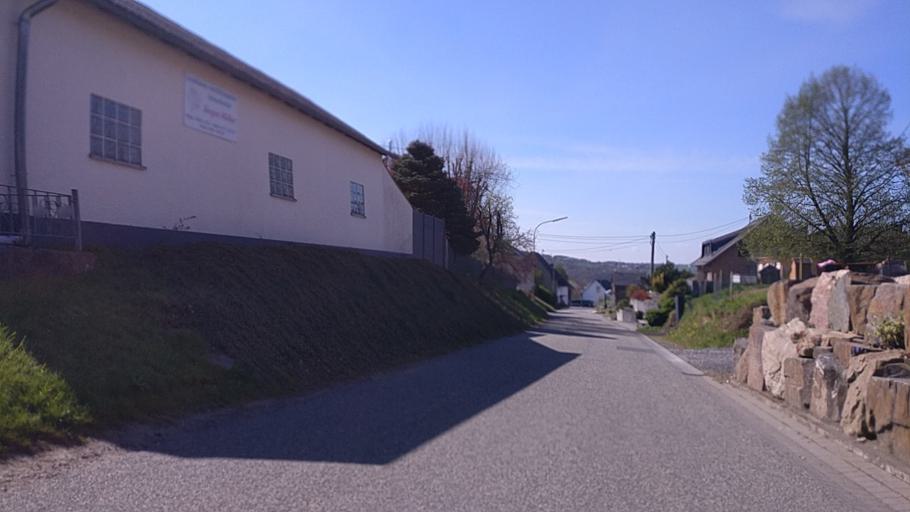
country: DE
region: Rheinland-Pfalz
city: Asbach
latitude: 50.6347
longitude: 7.4336
